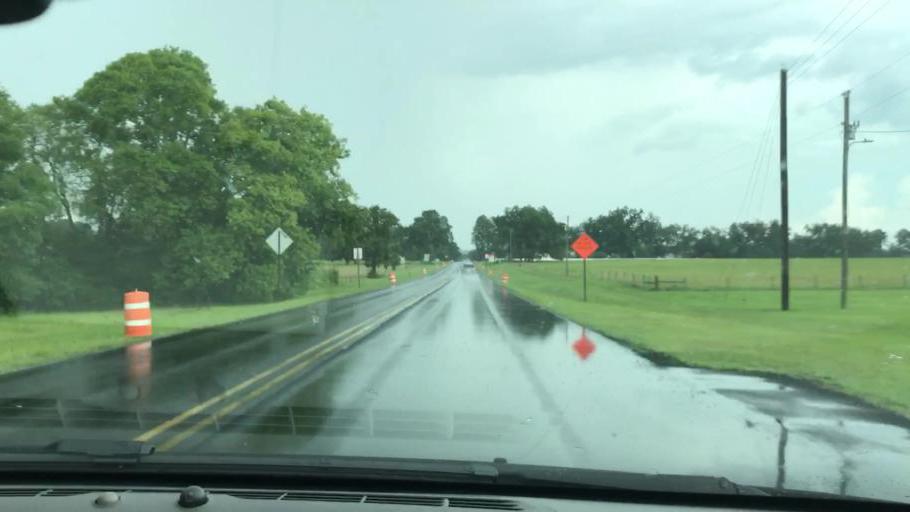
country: US
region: Georgia
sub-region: Clay County
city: Fort Gaines
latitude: 31.5396
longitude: -85.0208
